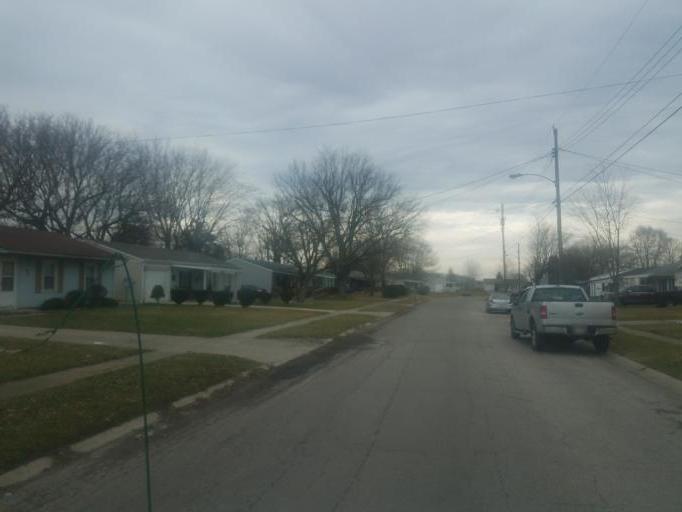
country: US
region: Ohio
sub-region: Marion County
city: Marion
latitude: 40.6054
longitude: -83.1177
